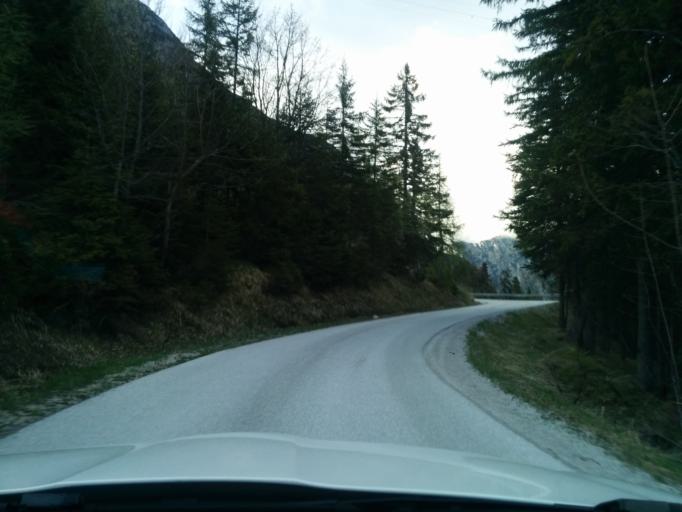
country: AT
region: Styria
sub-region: Politischer Bezirk Liezen
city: Aich
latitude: 47.4512
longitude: 13.8312
